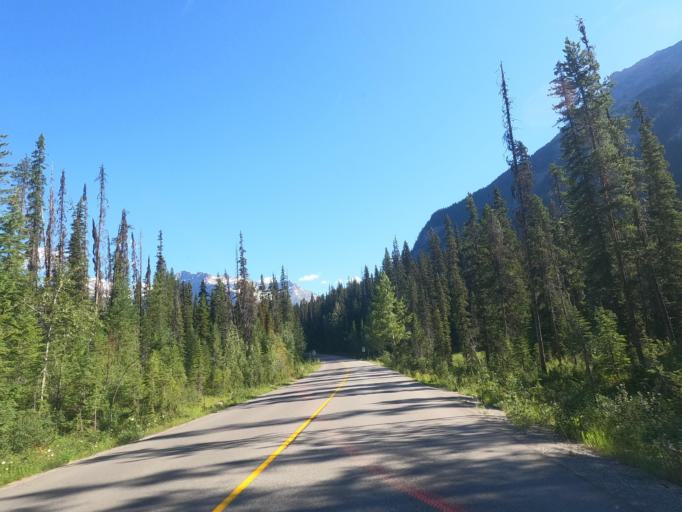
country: CA
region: Alberta
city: Lake Louise
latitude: 51.4105
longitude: -116.5343
